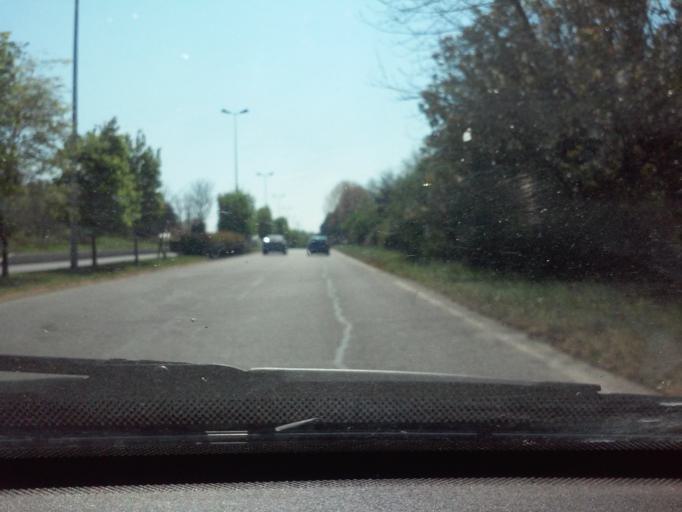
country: FR
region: Brittany
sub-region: Departement d'Ille-et-Vilaine
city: Saint-Malo
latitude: 48.6319
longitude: -1.9893
